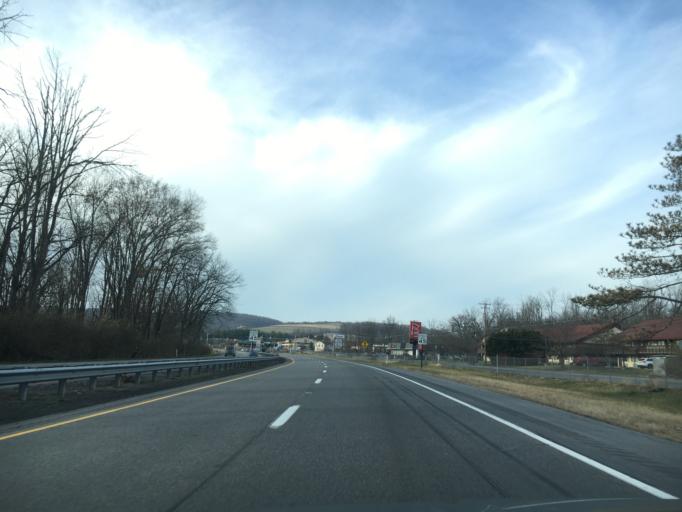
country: US
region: Pennsylvania
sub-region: Northumberland County
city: Riverside
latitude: 40.9928
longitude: -76.6375
